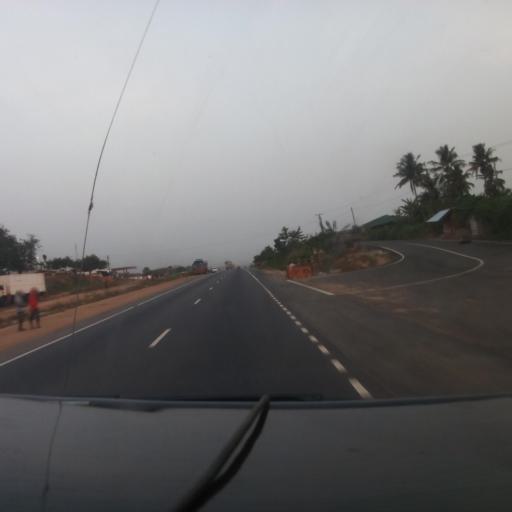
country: GH
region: Eastern
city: Nsawam
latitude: 5.8795
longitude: -0.3738
